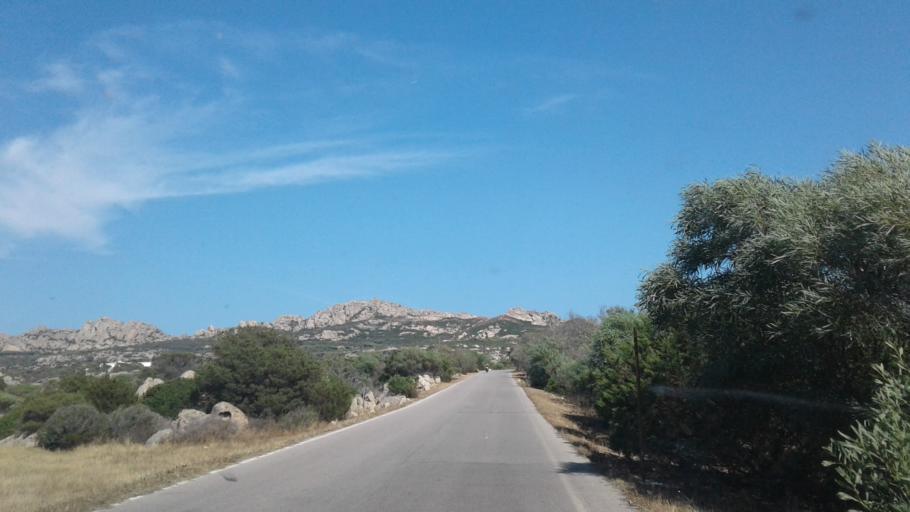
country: IT
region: Sardinia
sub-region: Provincia di Olbia-Tempio
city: La Maddalena
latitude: 41.2148
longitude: 9.4507
